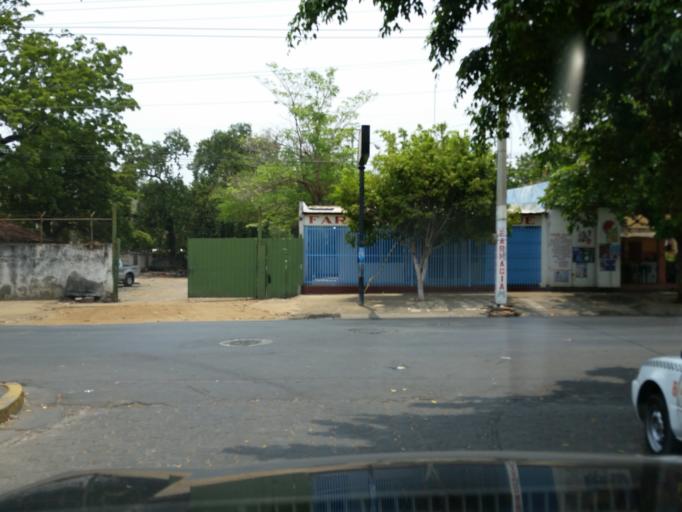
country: NI
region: Managua
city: Managua
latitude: 12.1501
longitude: -86.2493
